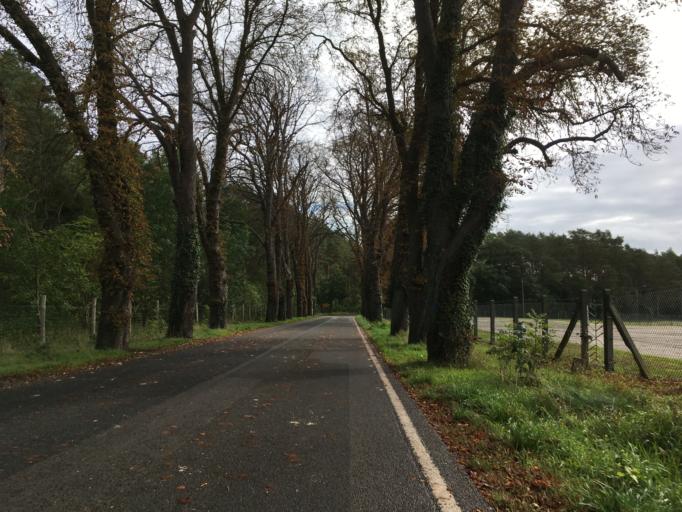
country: DE
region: Brandenburg
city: Oderberg
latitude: 52.8917
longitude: 14.0612
